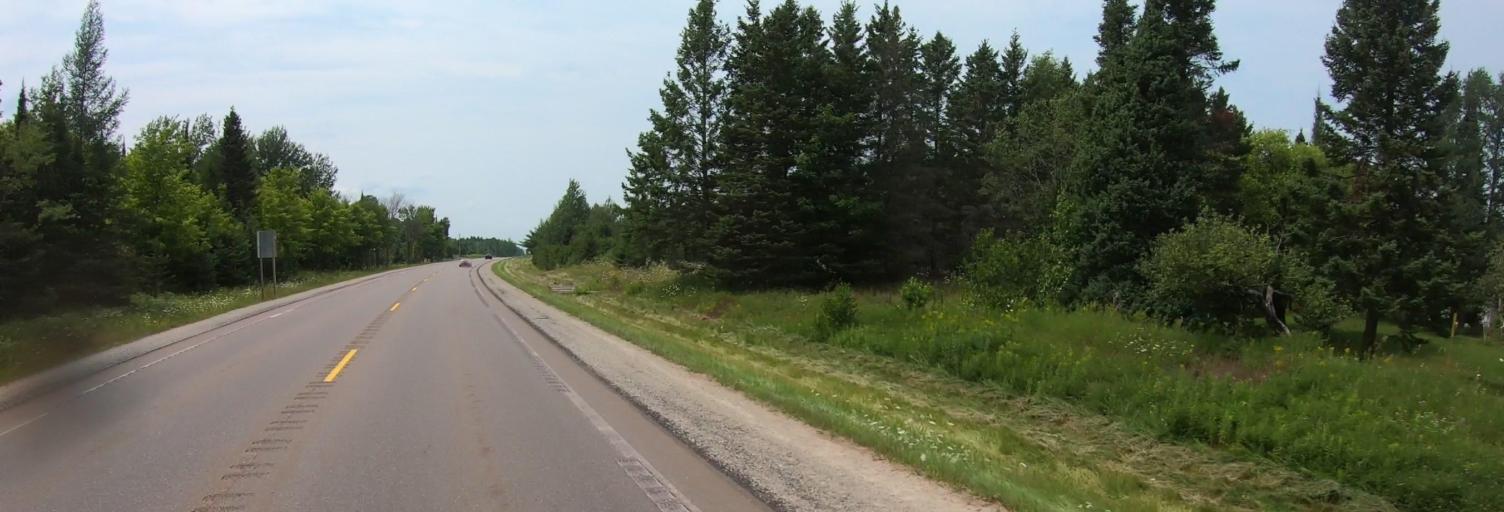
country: US
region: Michigan
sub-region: Marquette County
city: K. I. Sawyer Air Force Base
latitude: 46.3481
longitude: -87.0384
